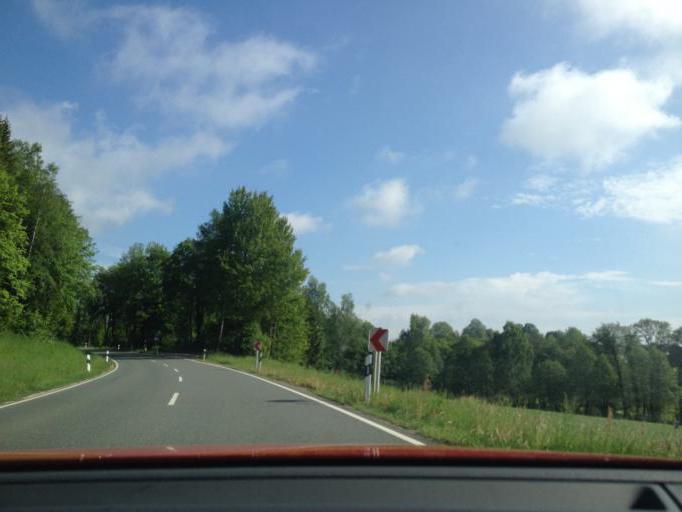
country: DE
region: Bavaria
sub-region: Upper Palatinate
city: Neusorg
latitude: 49.9122
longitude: 11.9712
